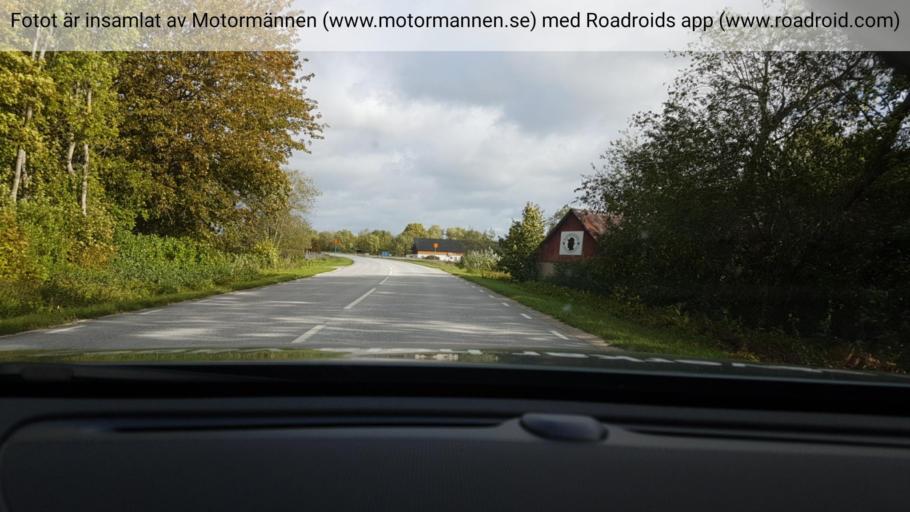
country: SE
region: Gotland
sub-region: Gotland
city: Slite
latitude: 57.7713
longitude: 18.7756
